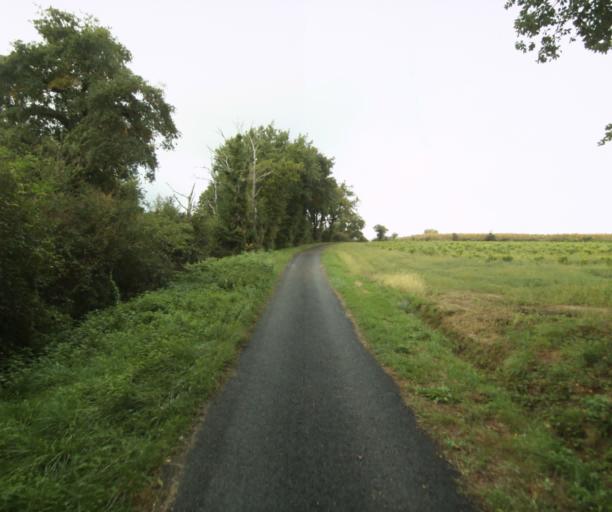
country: FR
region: Midi-Pyrenees
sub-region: Departement du Gers
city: Nogaro
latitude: 43.8282
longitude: -0.0919
